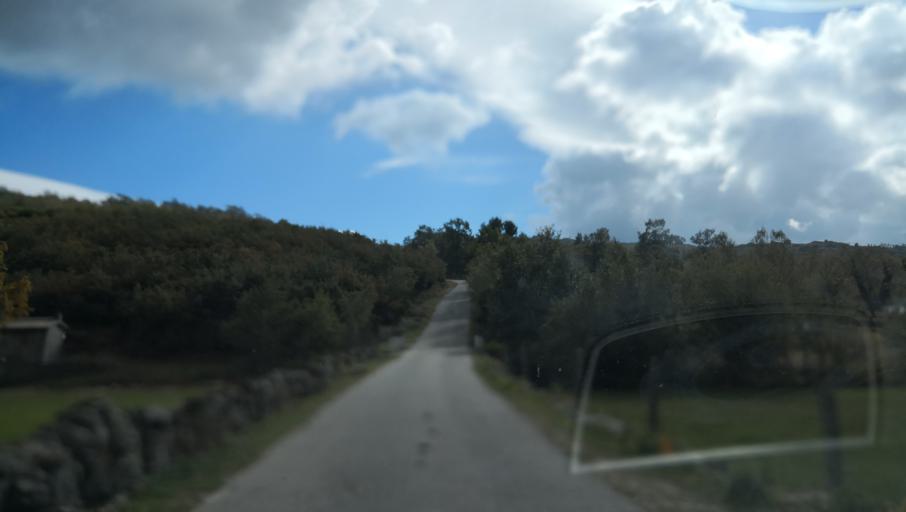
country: PT
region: Vila Real
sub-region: Vila Real
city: Vila Real
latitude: 41.3676
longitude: -7.7936
